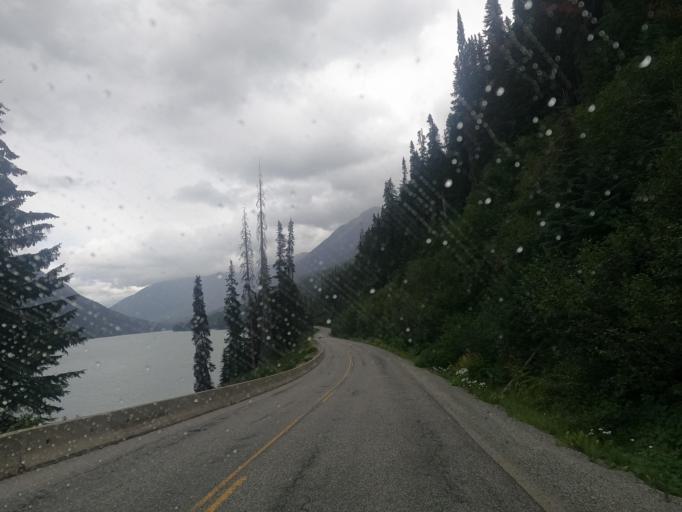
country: CA
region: British Columbia
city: Lillooet
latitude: 50.3957
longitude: -122.3263
